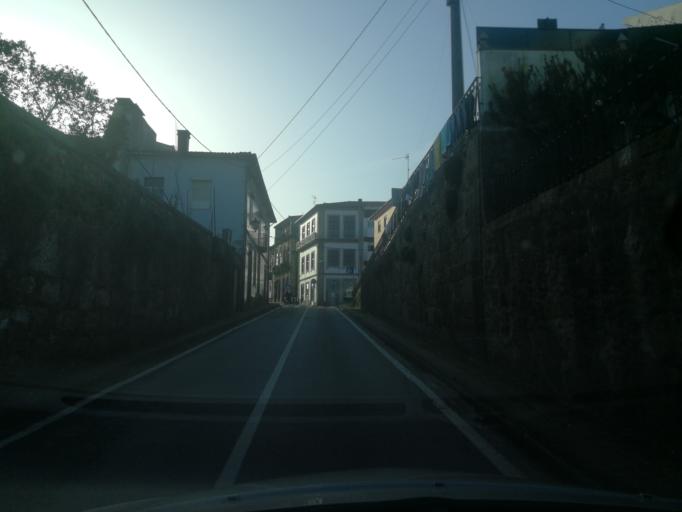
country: PT
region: Braga
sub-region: Barcelos
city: Barcelos
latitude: 41.5258
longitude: -8.6214
